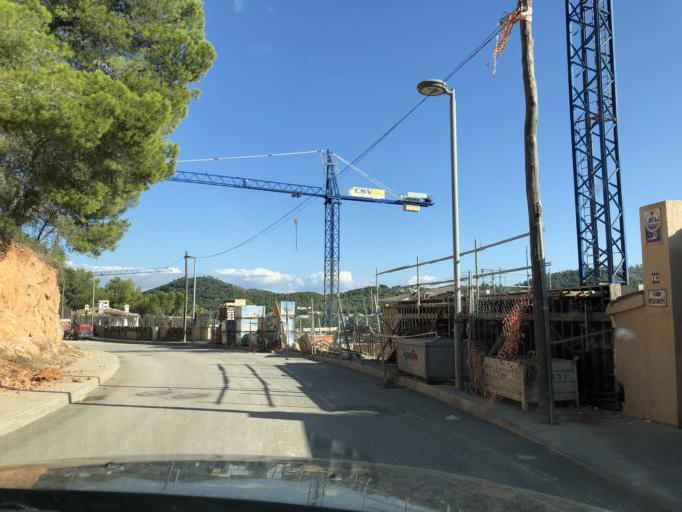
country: ES
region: Balearic Islands
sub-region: Illes Balears
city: Camp de Mar
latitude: 39.5397
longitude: 2.4116
